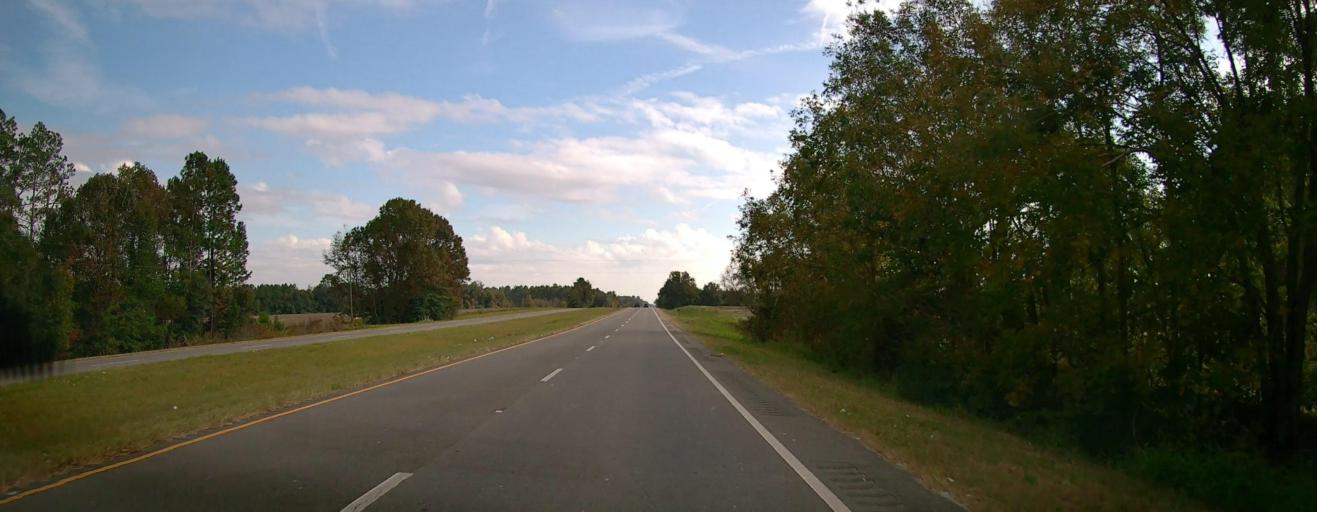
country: US
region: Georgia
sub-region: Thomas County
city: Meigs
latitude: 31.0263
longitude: -84.0604
